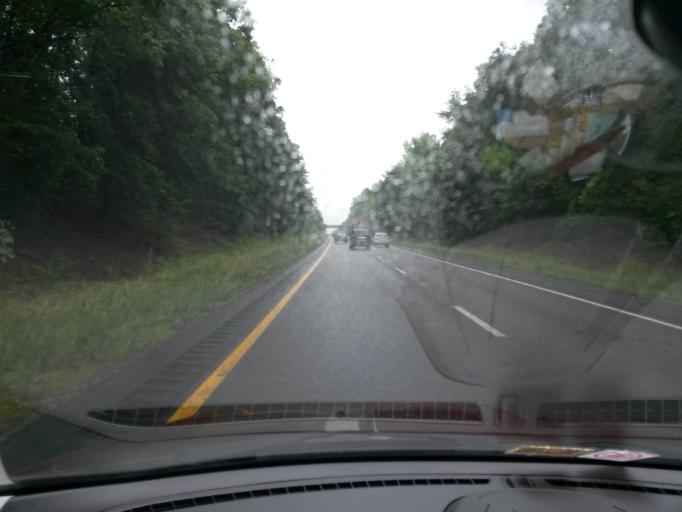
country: US
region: Virginia
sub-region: Goochland County
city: Goochland
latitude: 37.7614
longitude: -77.8646
